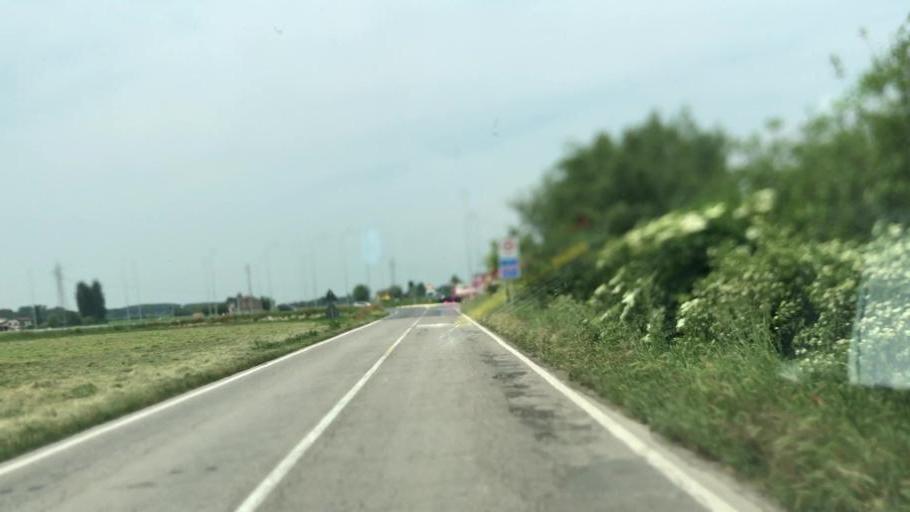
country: IT
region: Lombardy
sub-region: Provincia di Mantova
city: Campitello
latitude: 45.0815
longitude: 10.6006
